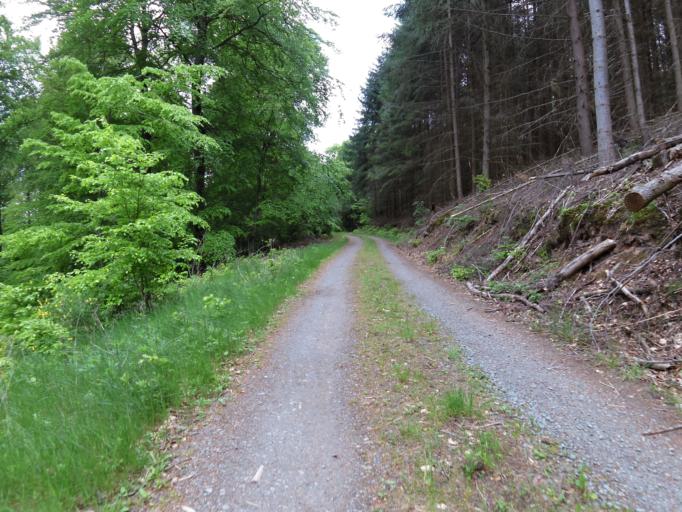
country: DE
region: Rheinland-Pfalz
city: Neidenfels
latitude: 49.4126
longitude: 8.0526
